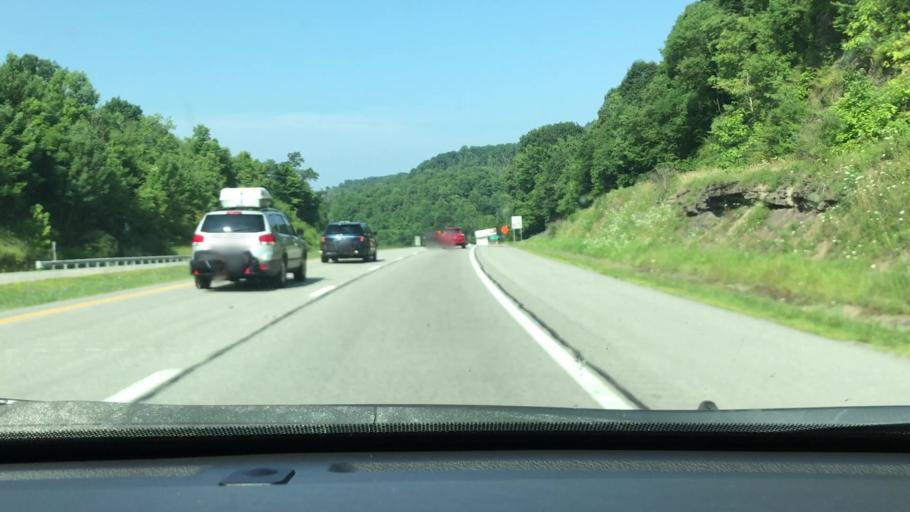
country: US
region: West Virginia
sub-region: Nicholas County
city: Summersville
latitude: 38.2674
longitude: -80.8447
